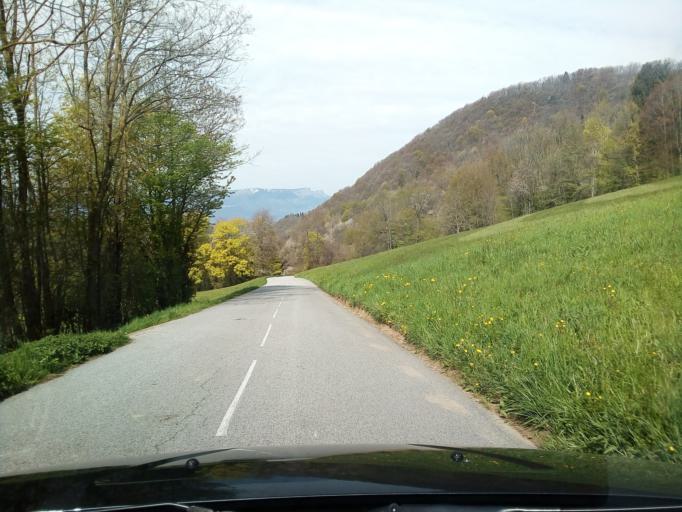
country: FR
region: Rhone-Alpes
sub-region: Departement de l'Isere
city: Herbeys
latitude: 45.1621
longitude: 5.8285
